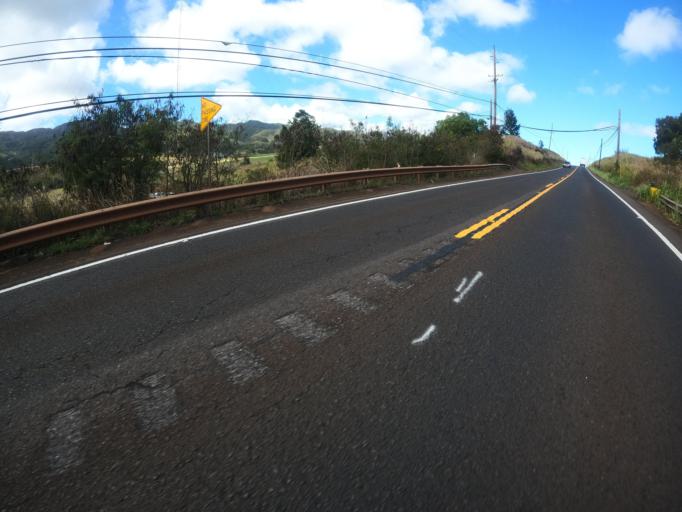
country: US
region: Hawaii
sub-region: Honolulu County
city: Waipi'o Acres
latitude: 21.4422
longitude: -158.0598
